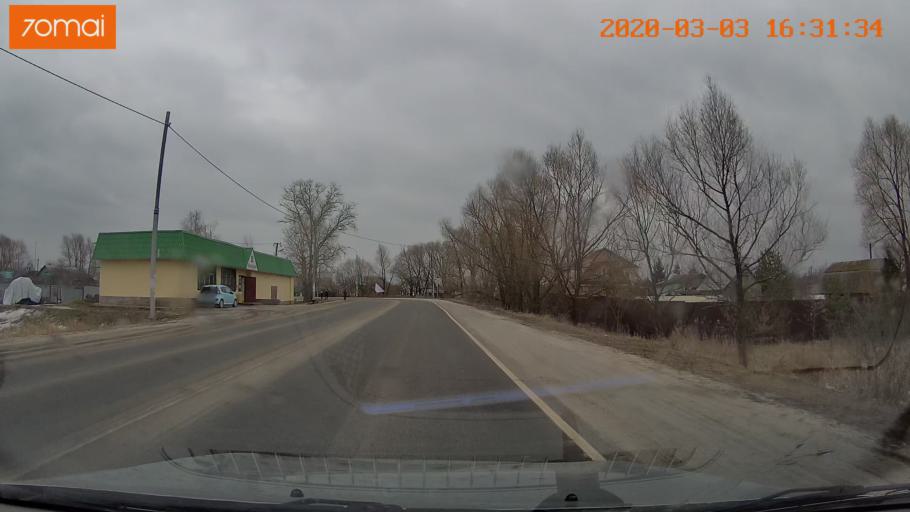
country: RU
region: Moskovskaya
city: Konobeyevo
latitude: 55.4244
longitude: 38.7263
